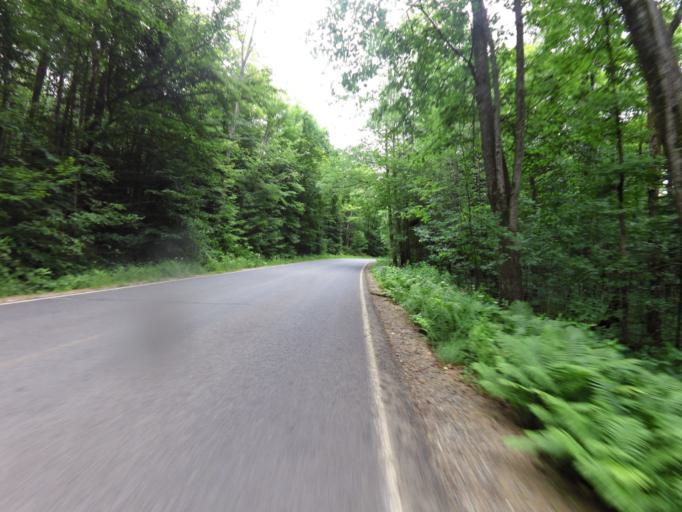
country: CA
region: Quebec
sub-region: Laurentides
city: Brownsburg-Chatham
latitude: 45.8863
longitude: -74.5793
